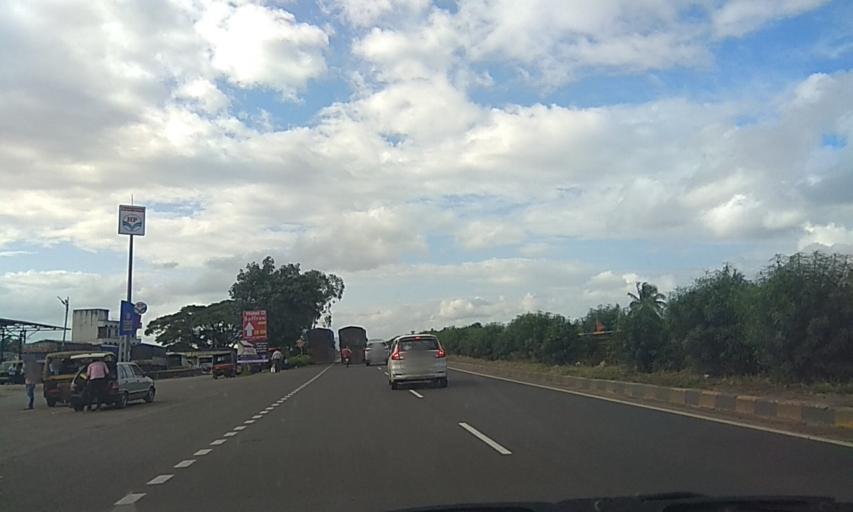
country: IN
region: Maharashtra
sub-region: Satara Division
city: Karad
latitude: 17.1253
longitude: 74.1915
